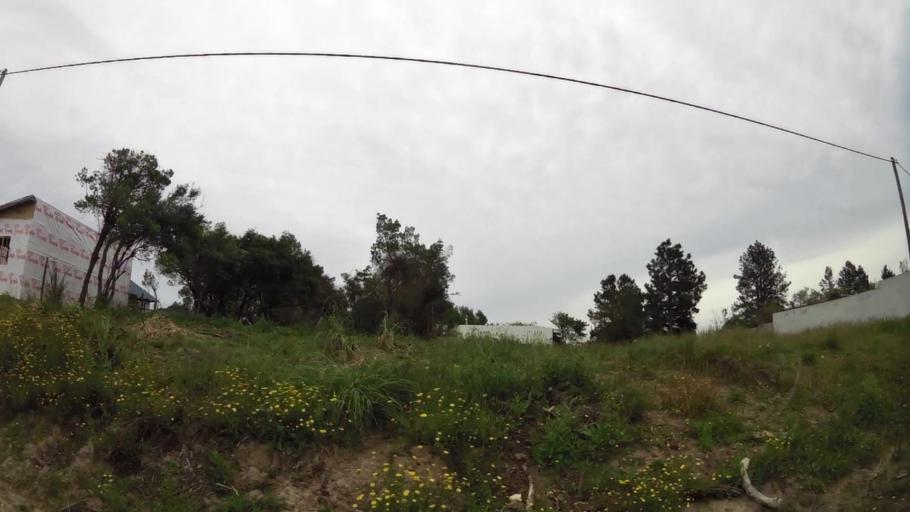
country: UY
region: Maldonado
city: Maldonado
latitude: -34.8977
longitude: -54.9908
